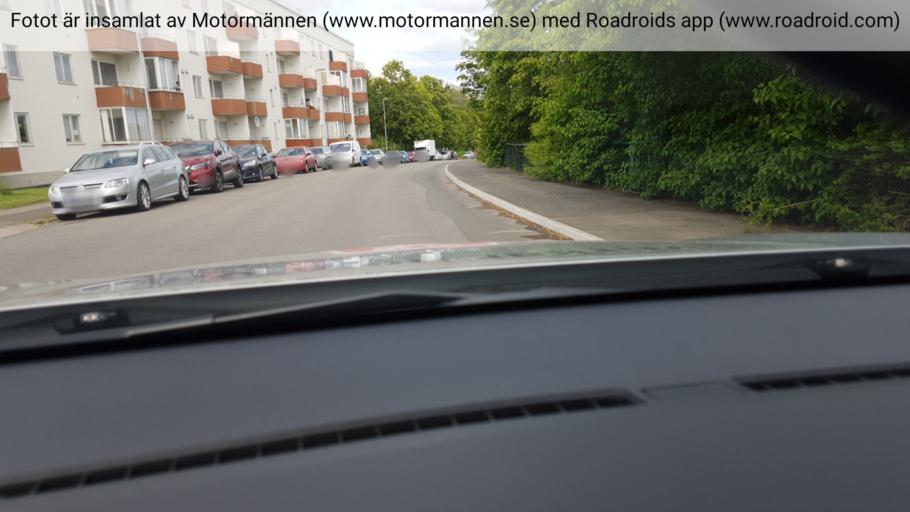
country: SE
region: Vaestra Goetaland
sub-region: Skovde Kommun
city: Skoevde
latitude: 58.3869
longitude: 13.8695
